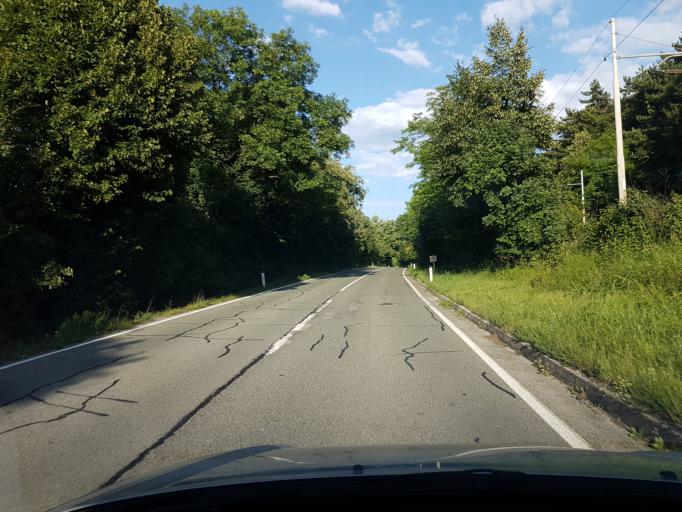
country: SI
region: Sezana
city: Sezana
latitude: 45.7042
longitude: 13.9089
